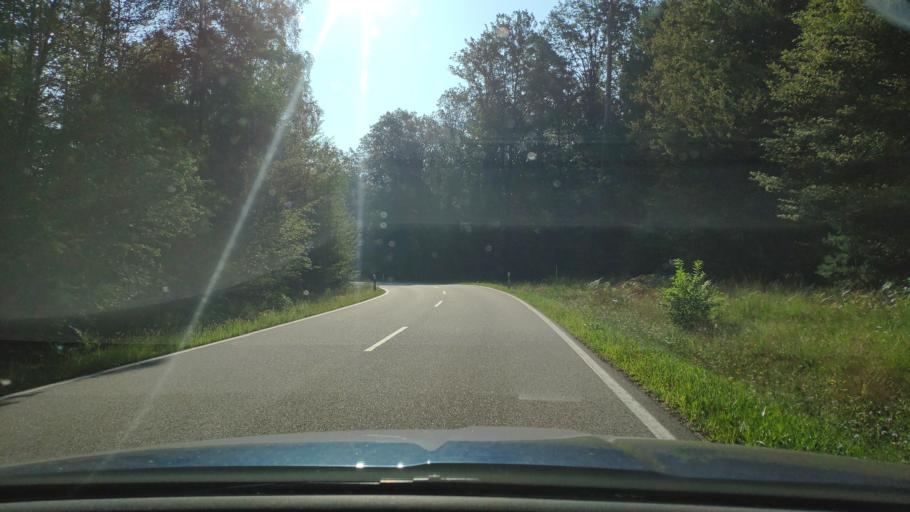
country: DE
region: Rheinland-Pfalz
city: Ludwigswinkel
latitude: 49.0700
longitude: 7.6807
